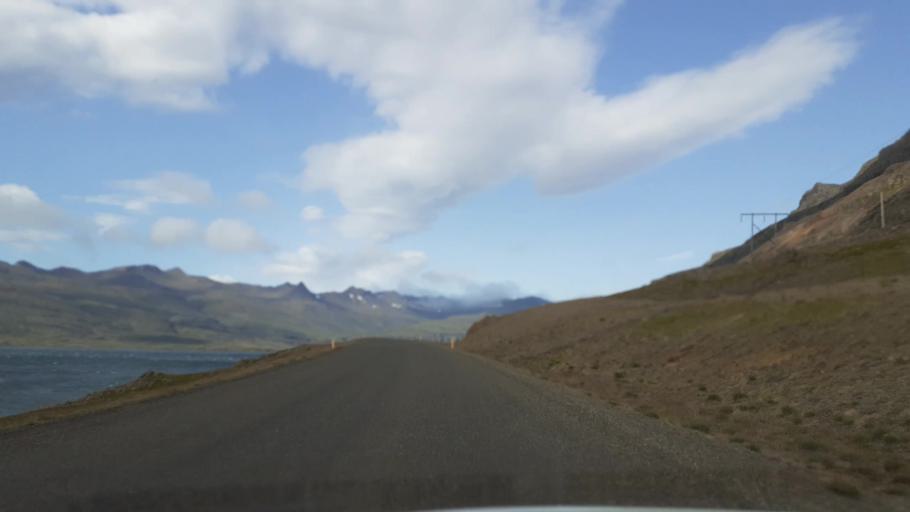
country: IS
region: East
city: Reydarfjoerdur
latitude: 64.6596
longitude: -14.3946
